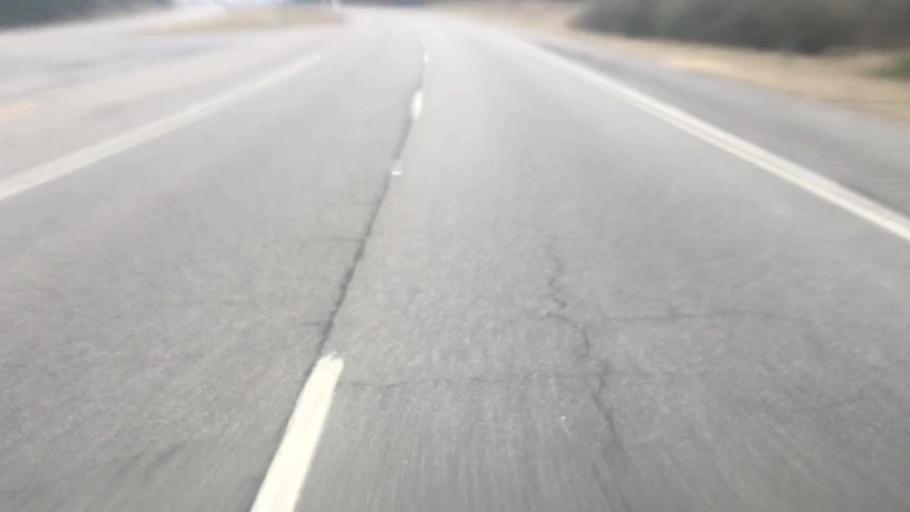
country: US
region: Alabama
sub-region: Walker County
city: Sumiton
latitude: 33.7482
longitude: -87.0557
